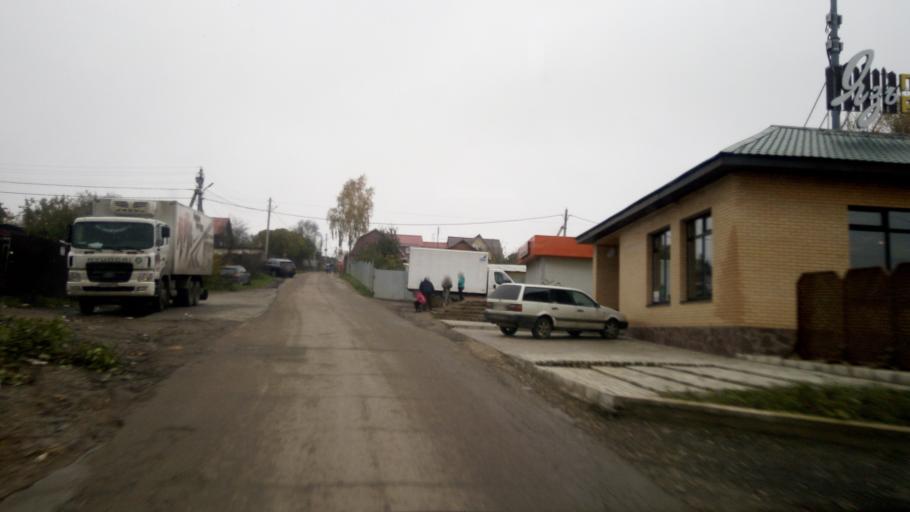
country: RU
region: Moskovskaya
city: Skhodnya
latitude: 55.9350
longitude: 37.2877
